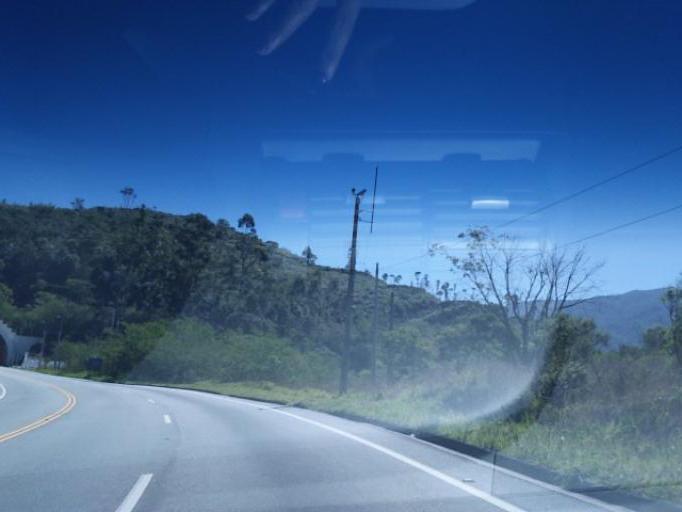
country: BR
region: Sao Paulo
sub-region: Campos Do Jordao
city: Campos do Jordao
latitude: -22.8469
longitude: -45.6147
